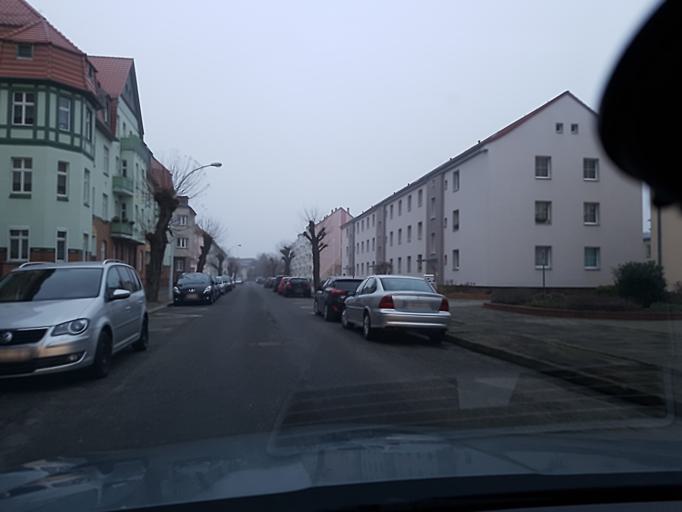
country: DE
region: Brandenburg
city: Finsterwalde
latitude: 51.6372
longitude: 13.7030
